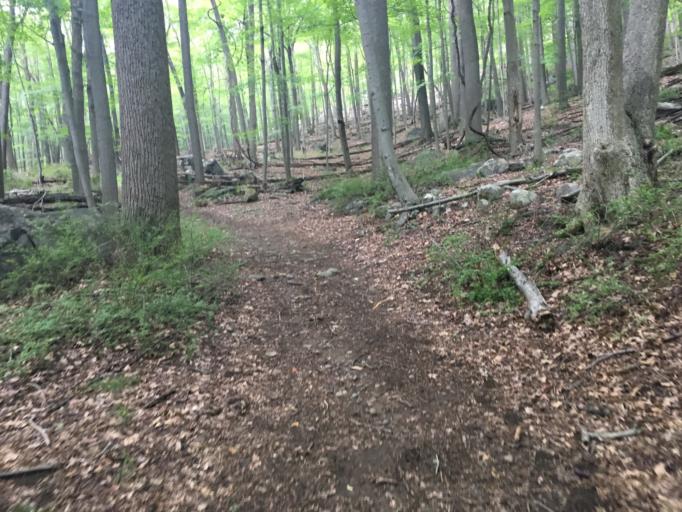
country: US
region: New York
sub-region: Orange County
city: Fort Montgomery
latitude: 41.3035
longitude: -73.9974
